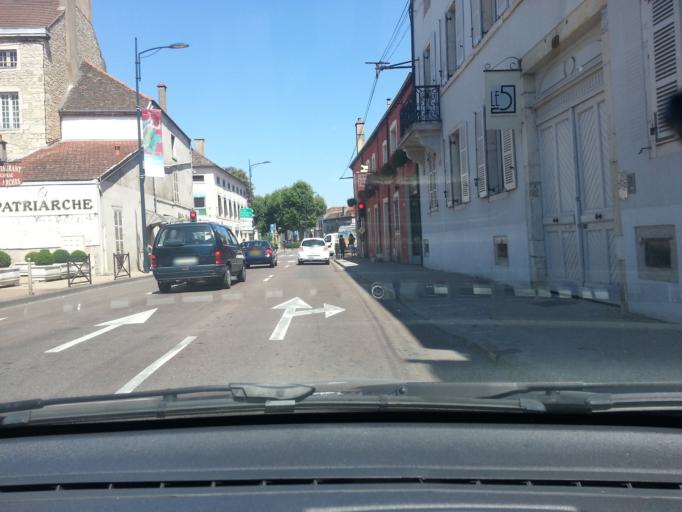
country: FR
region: Bourgogne
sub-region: Departement de la Cote-d'Or
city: Beaune
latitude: 47.0213
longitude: 4.8401
